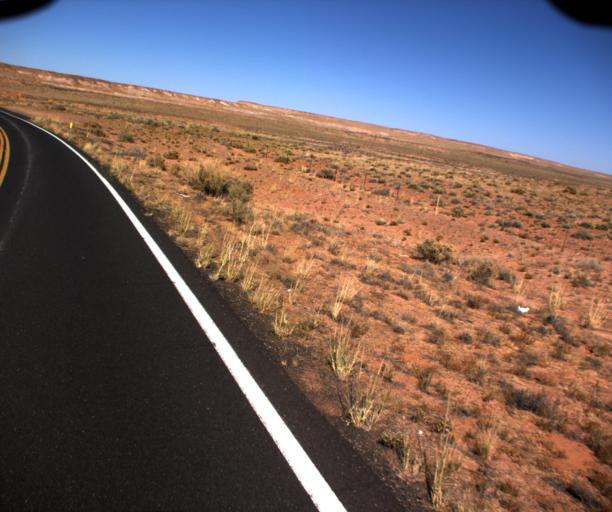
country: US
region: Arizona
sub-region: Coconino County
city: Tuba City
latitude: 36.0963
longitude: -111.1940
